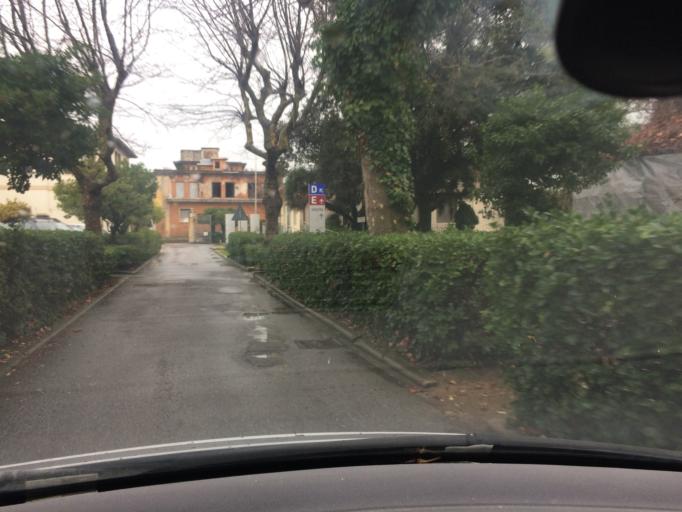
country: IT
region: Tuscany
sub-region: Provincia di Massa-Carrara
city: Massa
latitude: 44.0174
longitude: 10.0853
